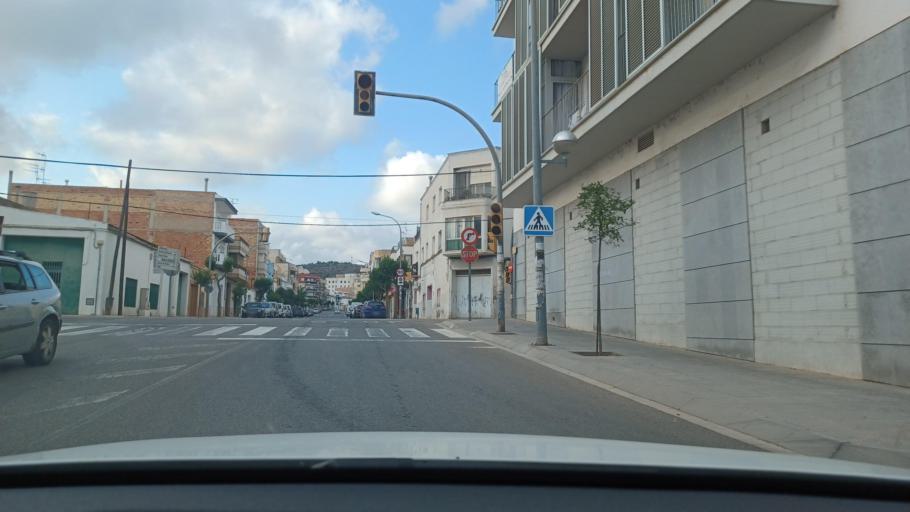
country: ES
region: Catalonia
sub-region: Provincia de Tarragona
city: Alcanar
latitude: 40.5410
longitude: 0.4778
